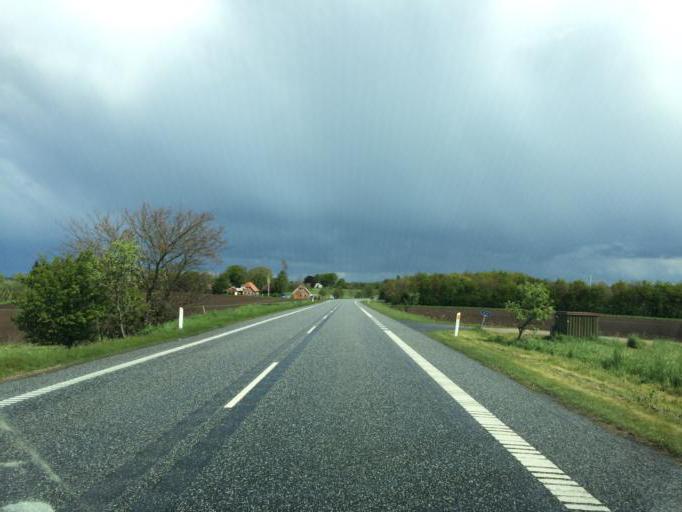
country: DK
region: Central Jutland
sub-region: Skive Kommune
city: Hojslev
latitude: 56.5680
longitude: 9.1167
